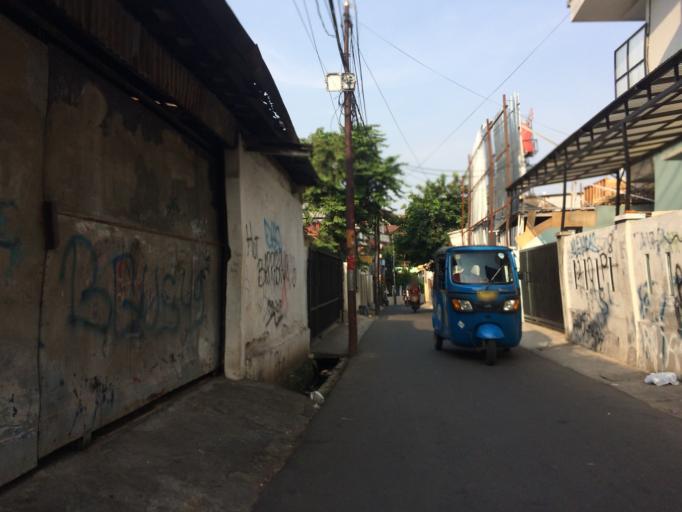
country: ID
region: Jakarta Raya
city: Jakarta
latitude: -6.2108
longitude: 106.8422
